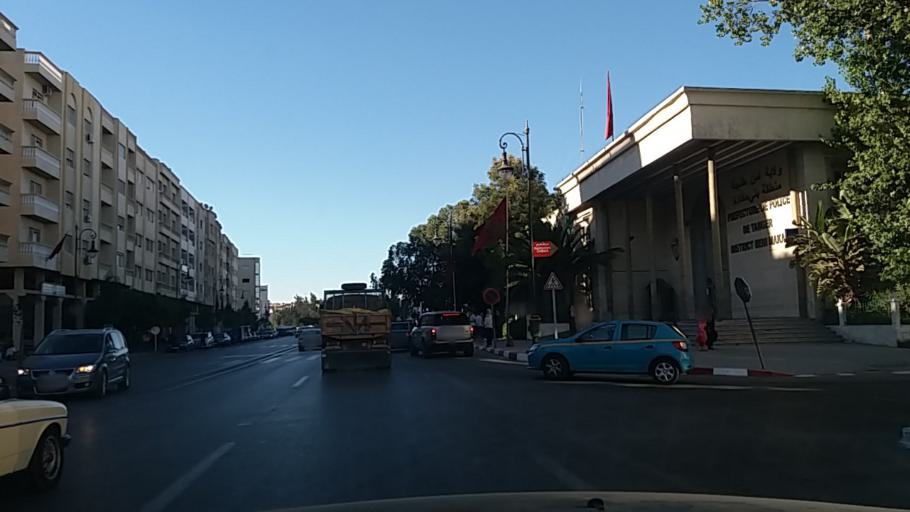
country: MA
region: Tanger-Tetouan
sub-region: Tanger-Assilah
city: Tangier
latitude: 35.7471
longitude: -5.7987
